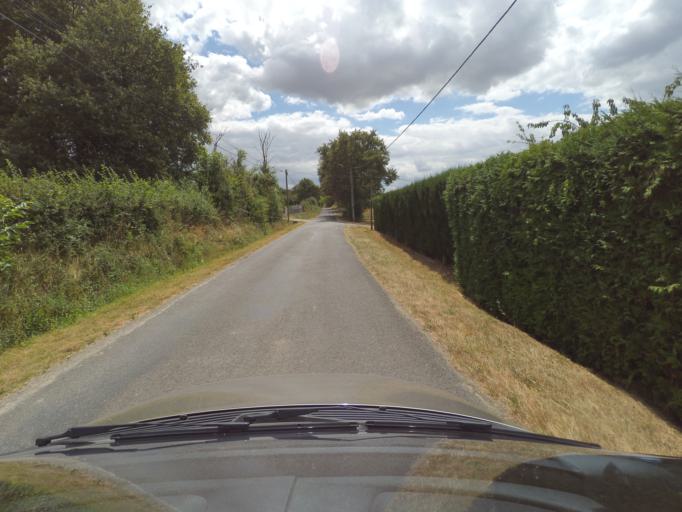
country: FR
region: Centre
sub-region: Departement de l'Indre
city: Belabre
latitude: 46.4609
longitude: 1.0585
